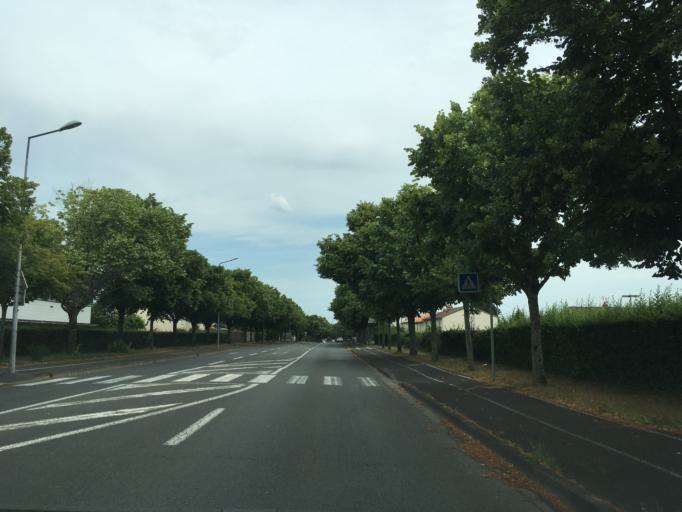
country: FR
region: Poitou-Charentes
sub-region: Departement des Deux-Sevres
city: Niort
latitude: 46.3112
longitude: -0.4765
